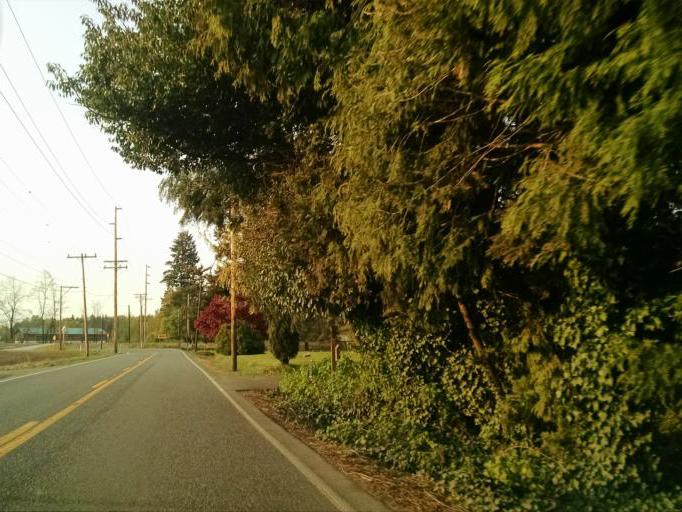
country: US
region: Washington
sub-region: Whatcom County
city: Nooksack
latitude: 48.8531
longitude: -122.2880
